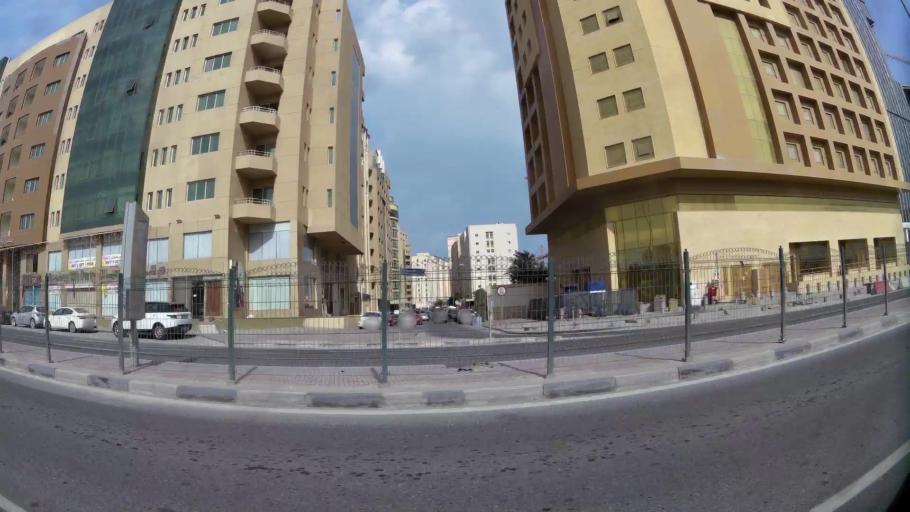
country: QA
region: Baladiyat ad Dawhah
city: Doha
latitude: 25.2863
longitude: 51.5166
